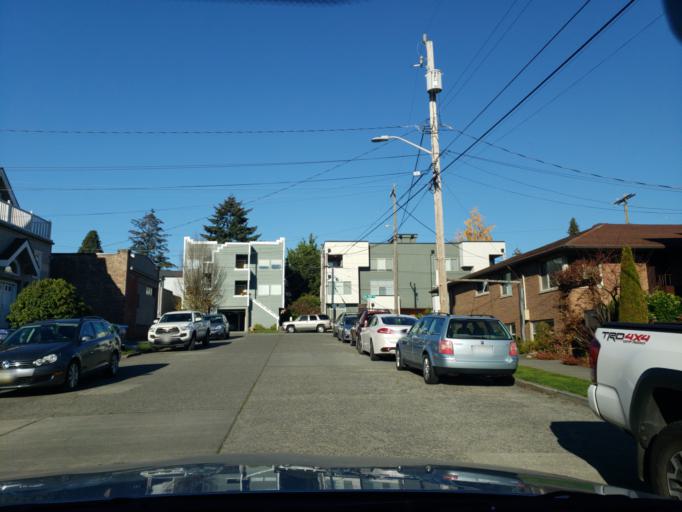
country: US
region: Washington
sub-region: King County
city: Shoreline
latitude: 47.6791
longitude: -122.3741
